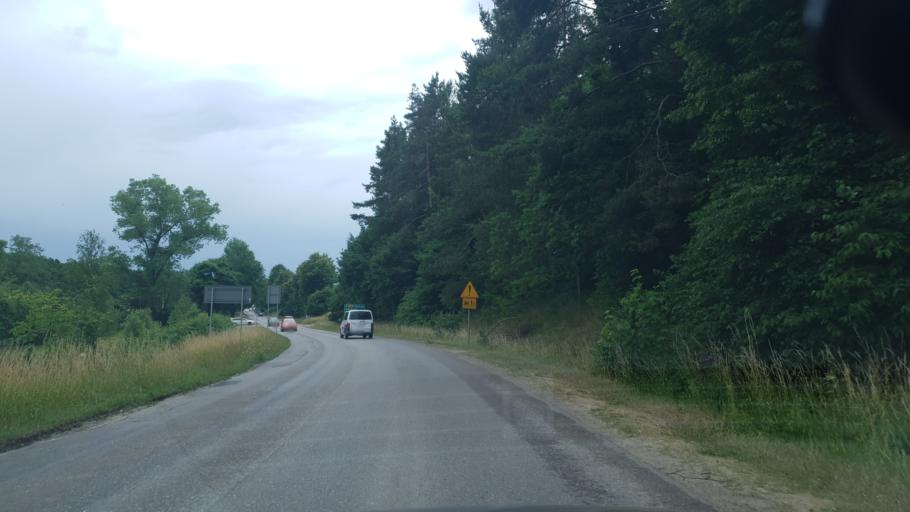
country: PL
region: Pomeranian Voivodeship
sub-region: Powiat kartuski
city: Przodkowo
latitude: 54.3628
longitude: 18.2616
